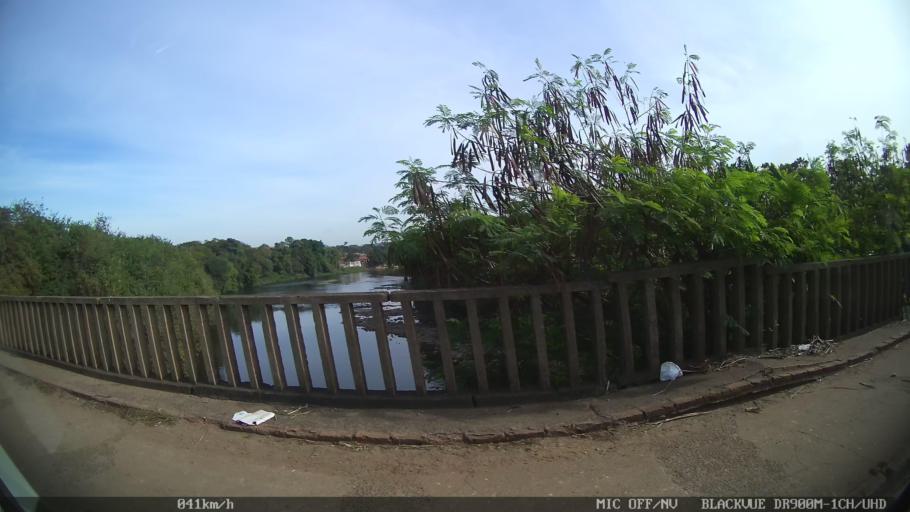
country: BR
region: Sao Paulo
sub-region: Piracicaba
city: Piracicaba
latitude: -22.6962
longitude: -47.6717
